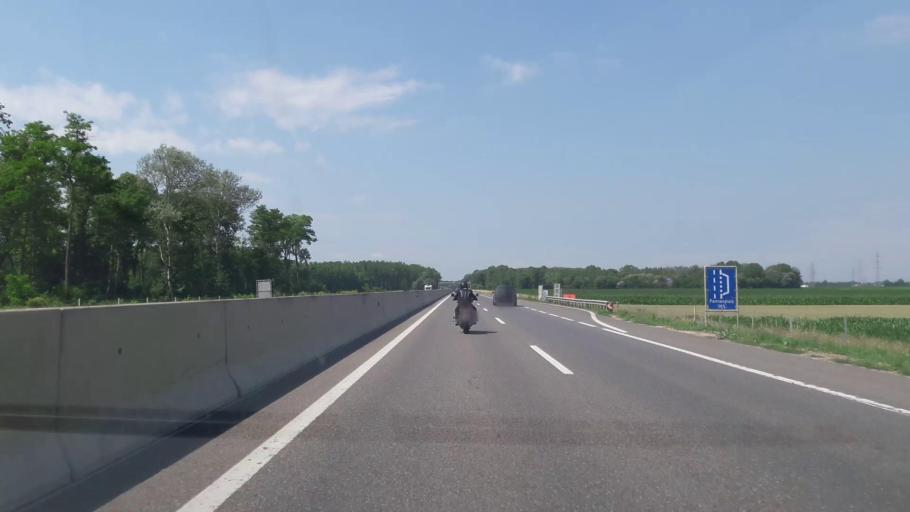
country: AT
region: Lower Austria
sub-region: Politischer Bezirk Korneuburg
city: Hausleiten
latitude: 48.3711
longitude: 16.1160
